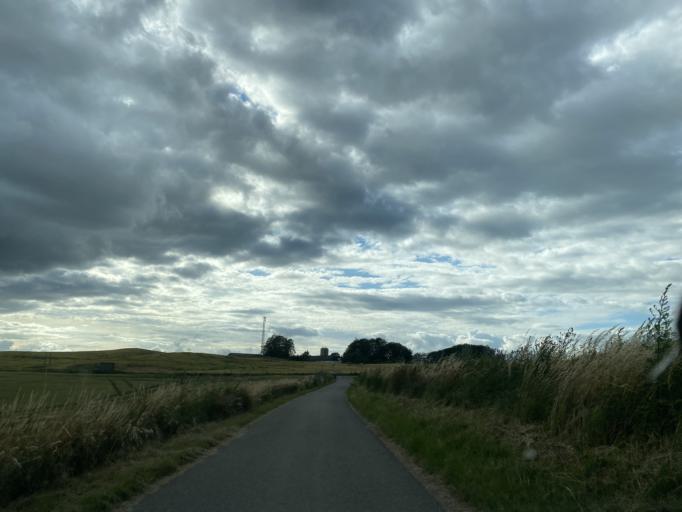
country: DK
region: Central Jutland
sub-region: Syddjurs Kommune
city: Ronde
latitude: 56.2883
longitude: 10.5745
